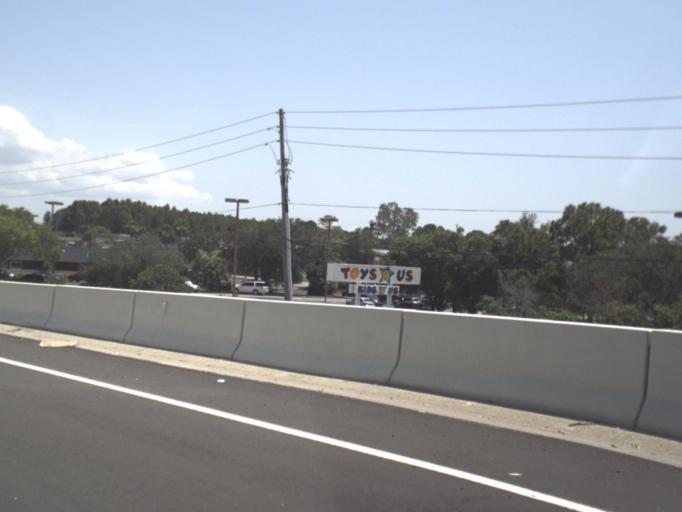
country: US
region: Florida
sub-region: Pinellas County
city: Dunedin
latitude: 28.0133
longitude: -82.7356
